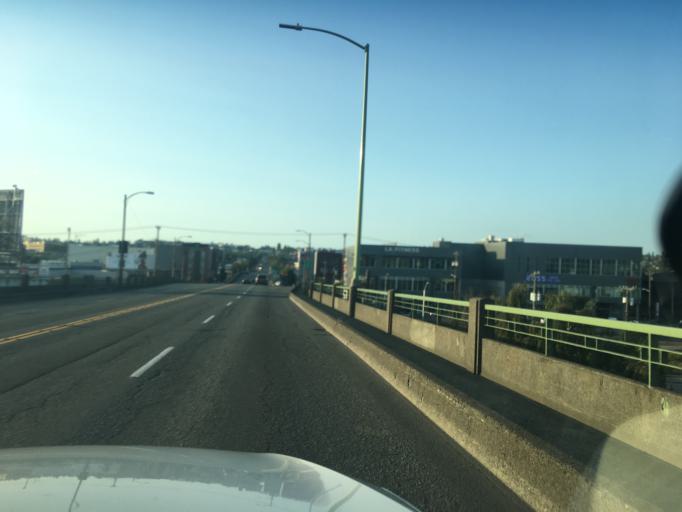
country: US
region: Washington
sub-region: King County
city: Seattle
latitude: 47.6608
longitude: -122.3762
